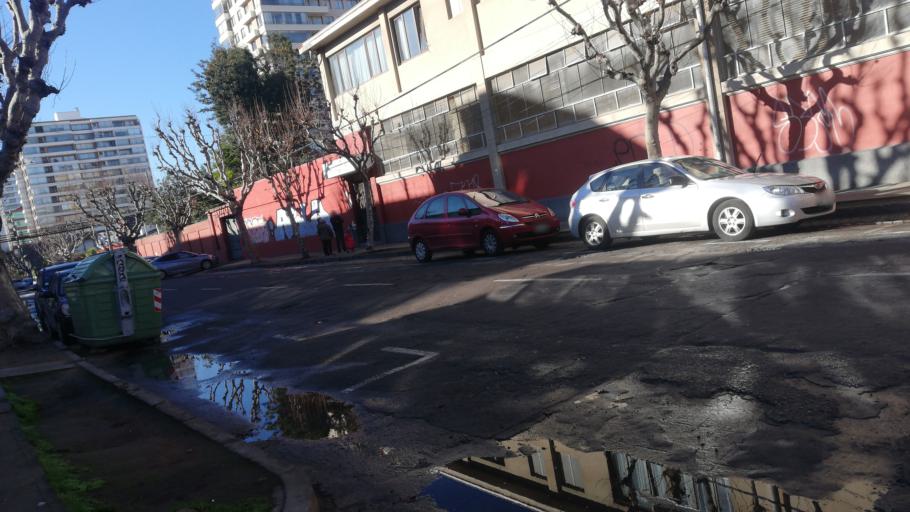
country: CL
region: Valparaiso
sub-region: Provincia de Valparaiso
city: Vina del Mar
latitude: -33.0185
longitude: -71.5502
